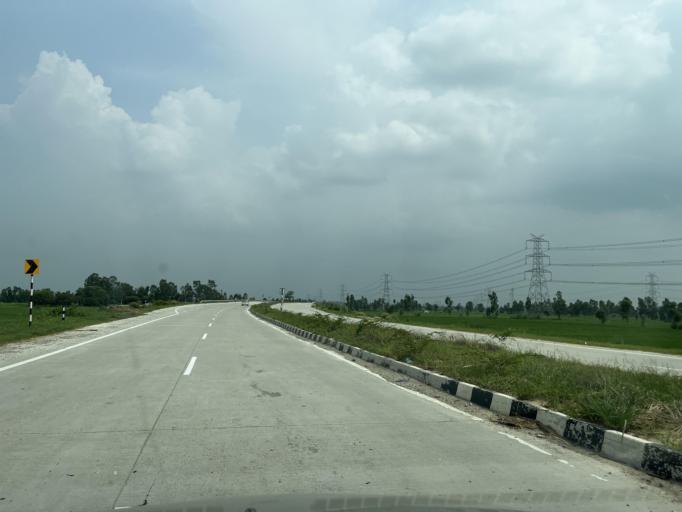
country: IN
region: Uttarakhand
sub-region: Udham Singh Nagar
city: Jaspur
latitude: 29.2906
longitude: 78.8508
